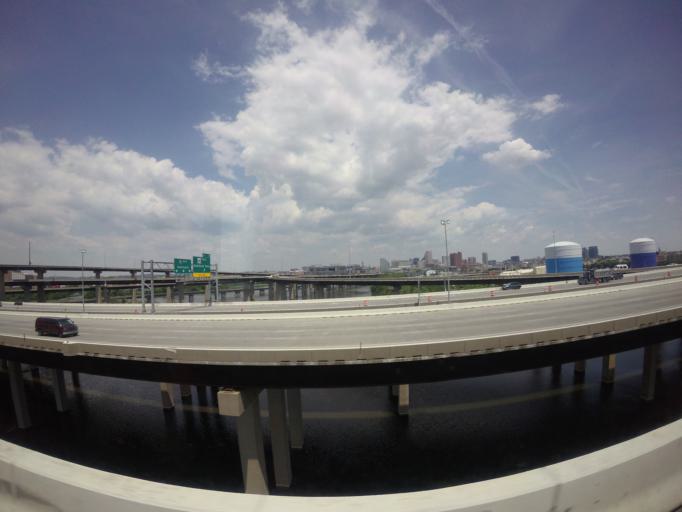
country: US
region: Maryland
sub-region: City of Baltimore
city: Baltimore
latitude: 39.2668
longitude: -76.6220
